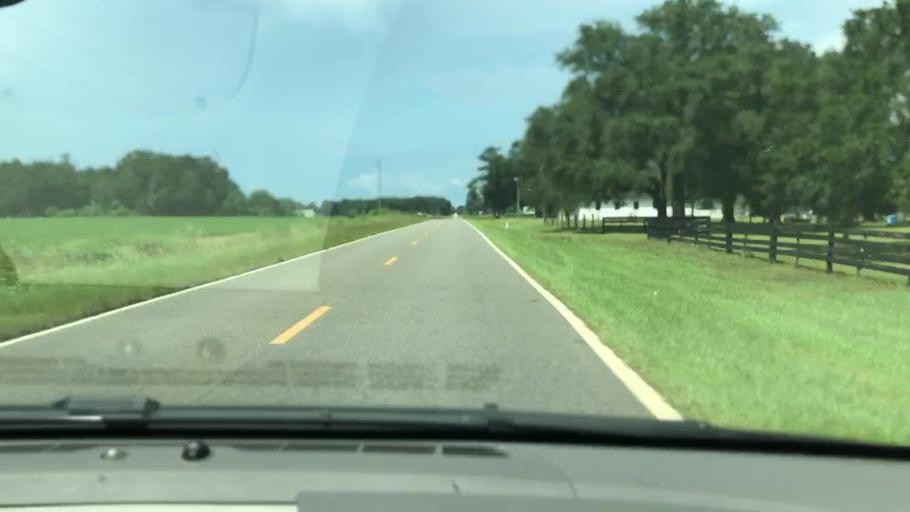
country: US
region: Georgia
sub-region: Seminole County
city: Donalsonville
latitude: 31.1092
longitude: -84.9959
